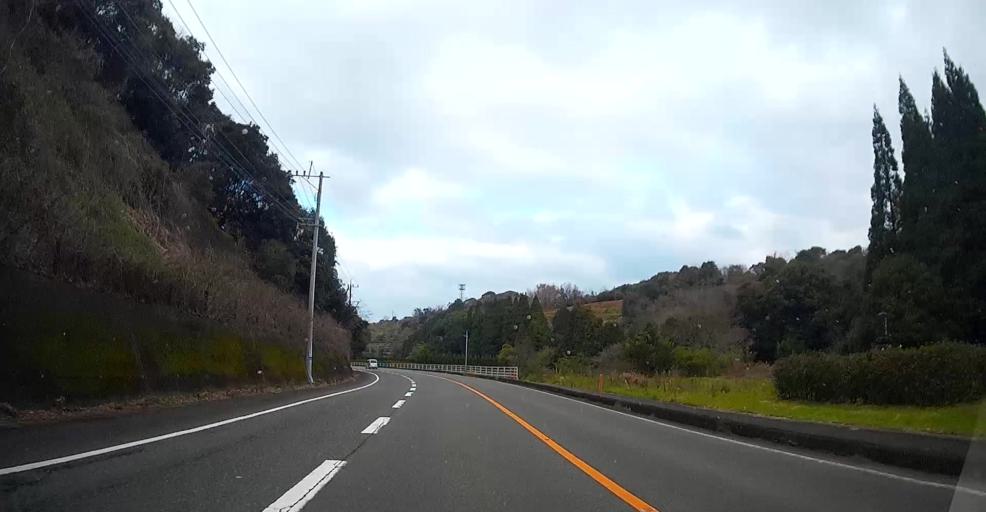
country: JP
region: Kumamoto
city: Hondo
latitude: 32.4966
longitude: 130.2991
